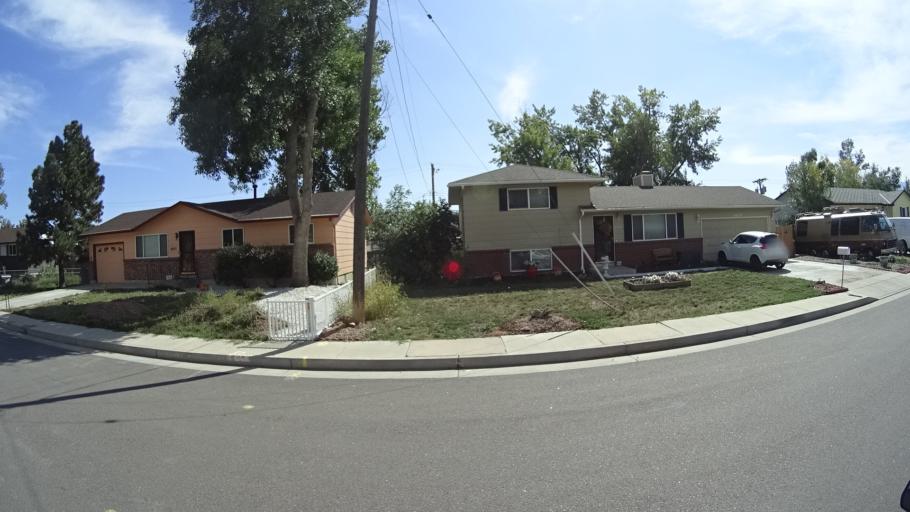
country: US
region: Colorado
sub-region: El Paso County
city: Cimarron Hills
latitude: 38.8917
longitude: -104.7652
